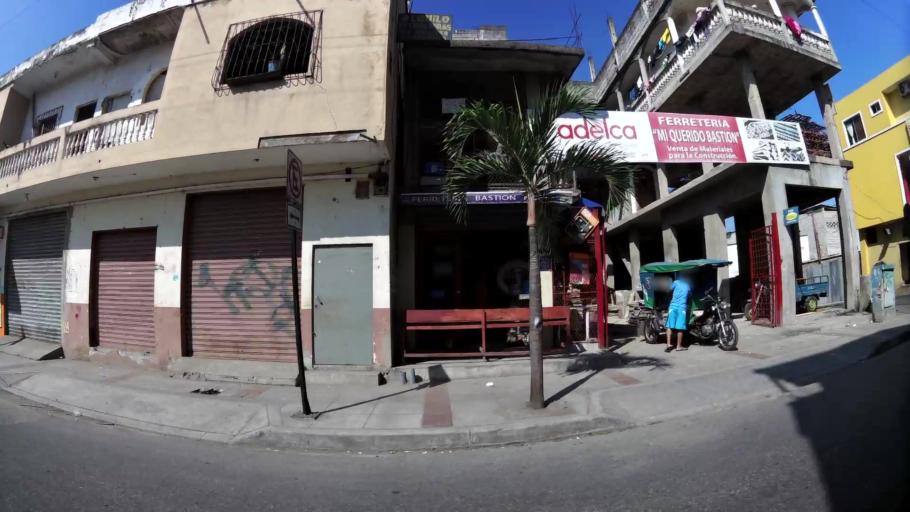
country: EC
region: Guayas
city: Eloy Alfaro
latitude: -2.0999
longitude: -79.9301
